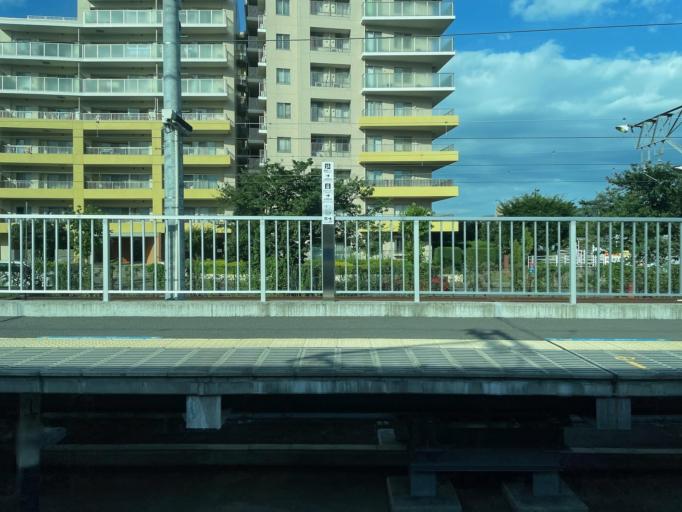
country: JP
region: Kanagawa
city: Odawara
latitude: 35.3270
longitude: 139.1357
